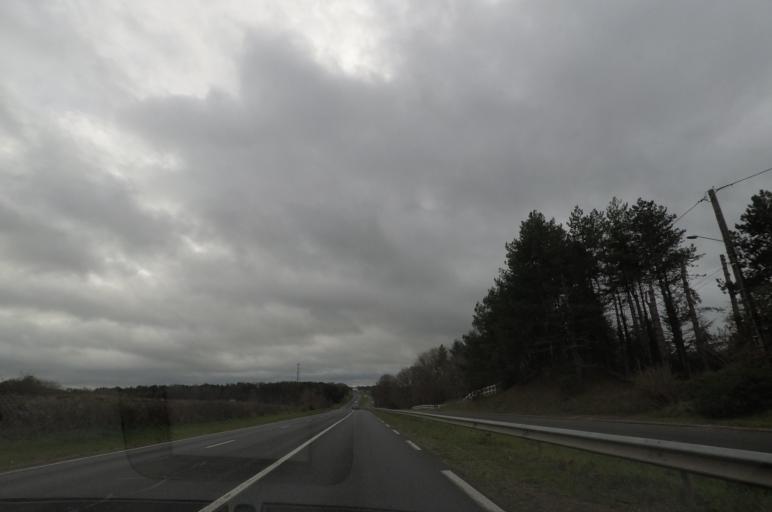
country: FR
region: Centre
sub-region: Departement du Loir-et-Cher
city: Saint-Sulpice-de-Pommeray
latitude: 47.6558
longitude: 1.2706
